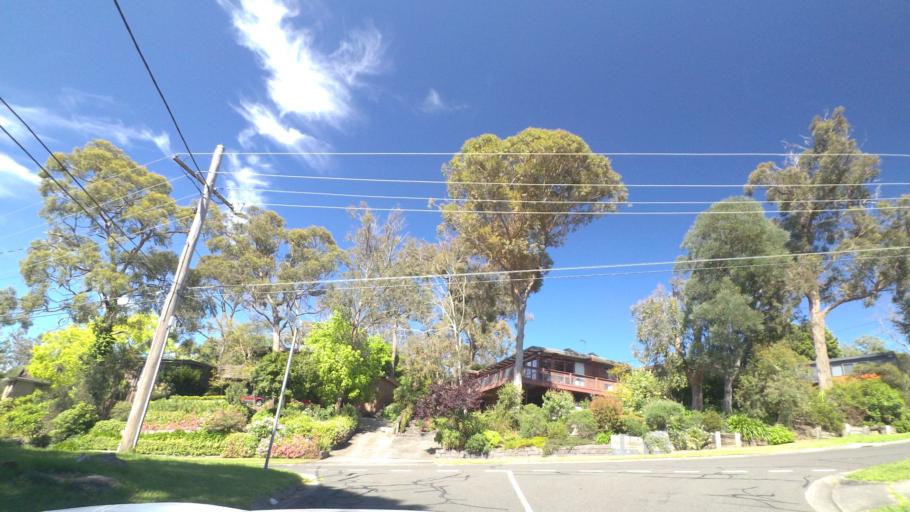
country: AU
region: Victoria
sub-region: Maroondah
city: Ringwood East
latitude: -37.8172
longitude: 145.2588
